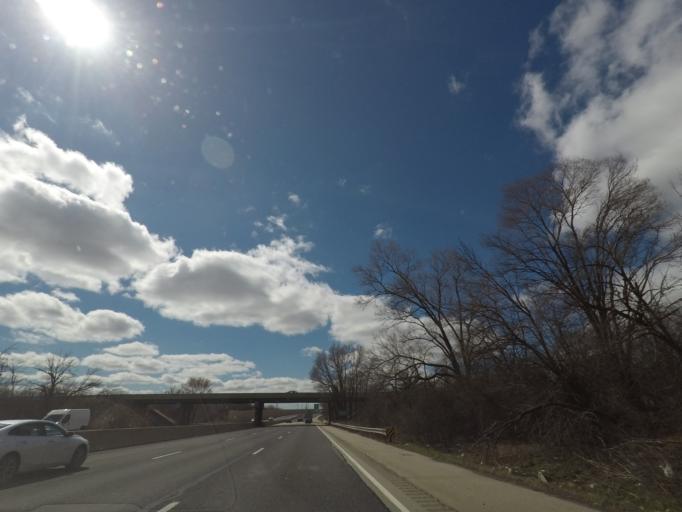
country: US
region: Illinois
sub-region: Will County
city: Crystal Lawns
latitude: 41.5954
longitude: -88.1632
